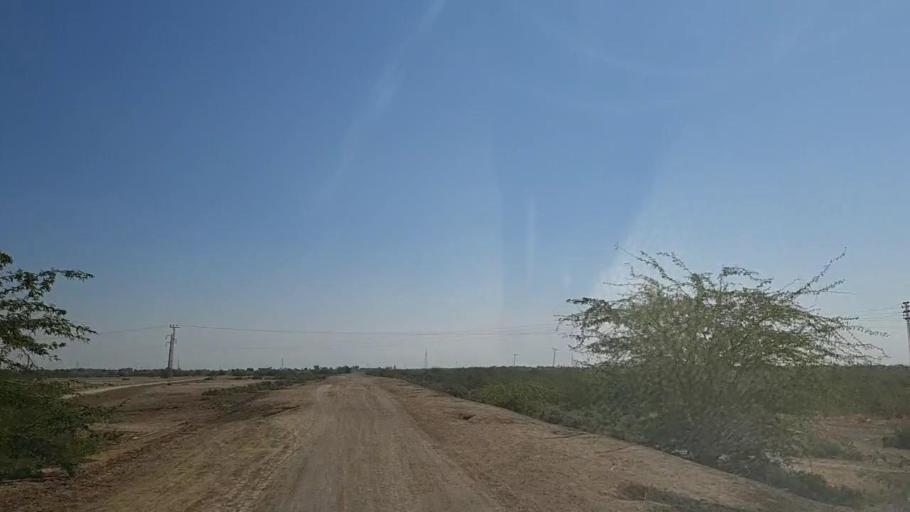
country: PK
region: Sindh
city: Samaro
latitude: 25.3053
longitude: 69.4798
